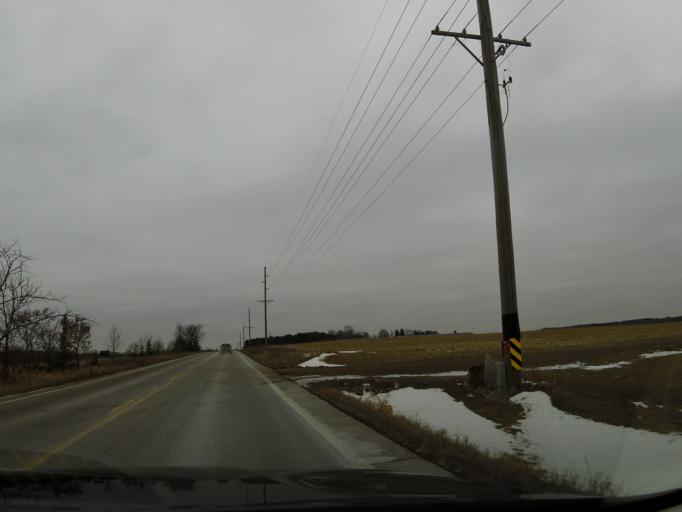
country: US
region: Minnesota
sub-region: Hennepin County
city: Independence
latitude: 45.0121
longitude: -93.7273
